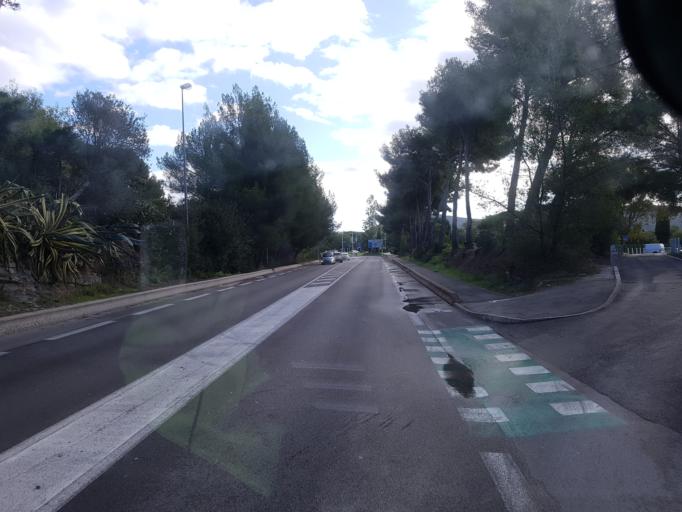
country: FR
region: Provence-Alpes-Cote d'Azur
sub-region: Departement du Var
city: Saint-Cyr-sur-Mer
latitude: 43.1833
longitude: 5.6877
